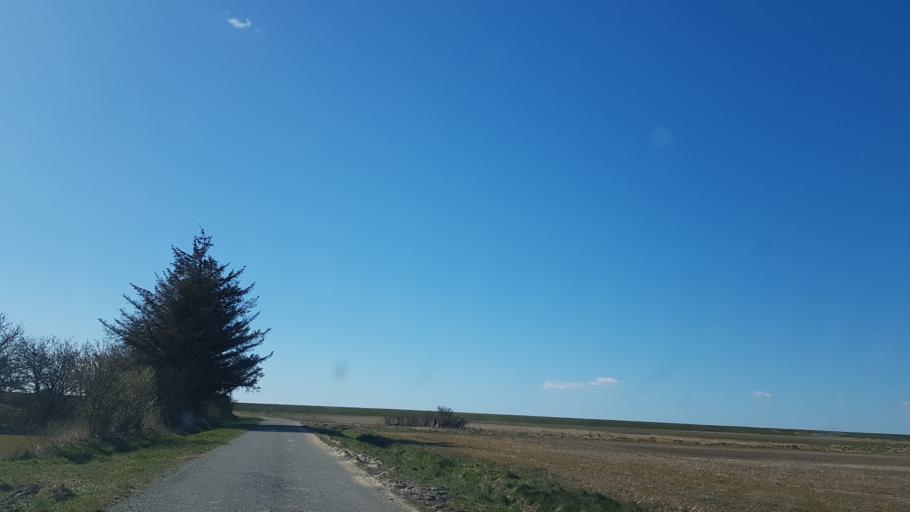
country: DK
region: South Denmark
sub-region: Esbjerg Kommune
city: Ribe
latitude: 55.2596
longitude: 8.6714
